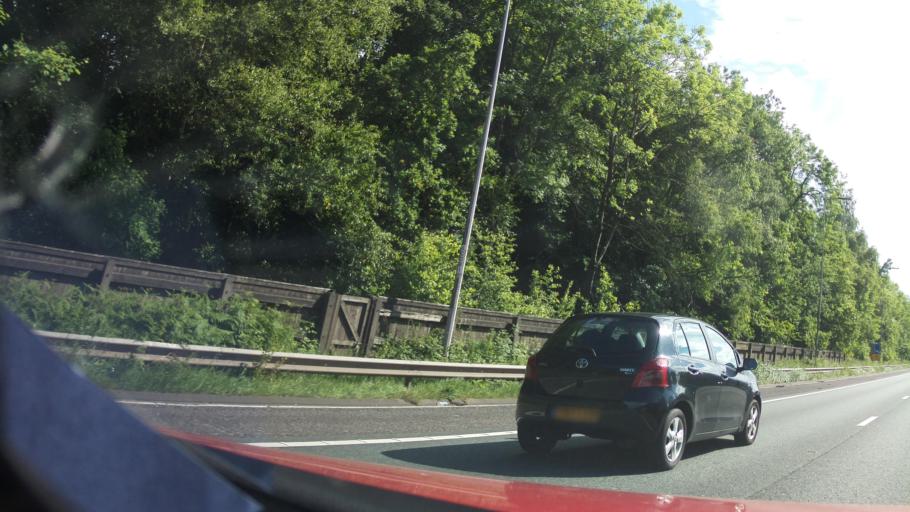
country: GB
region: England
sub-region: Manchester
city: Swinton
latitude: 53.5075
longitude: -2.3748
